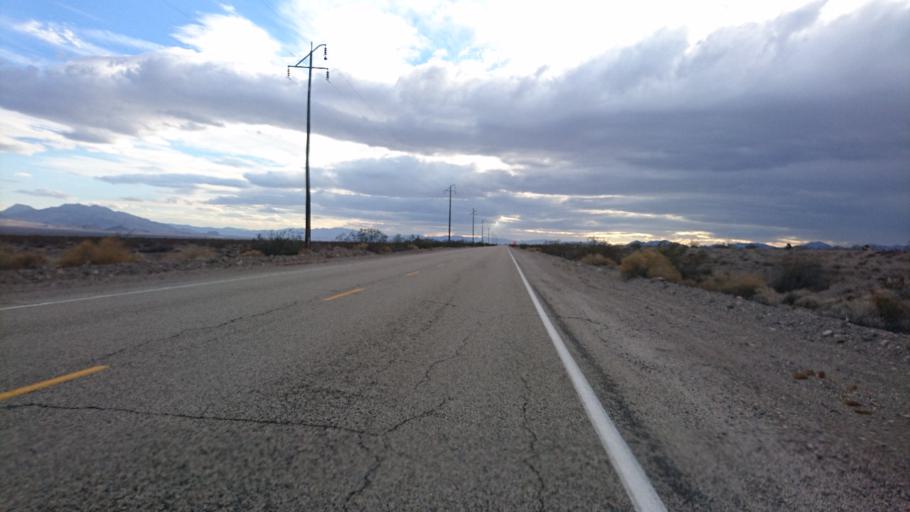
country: US
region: California
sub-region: San Bernardino County
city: Needles
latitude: 34.6583
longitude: -115.3573
